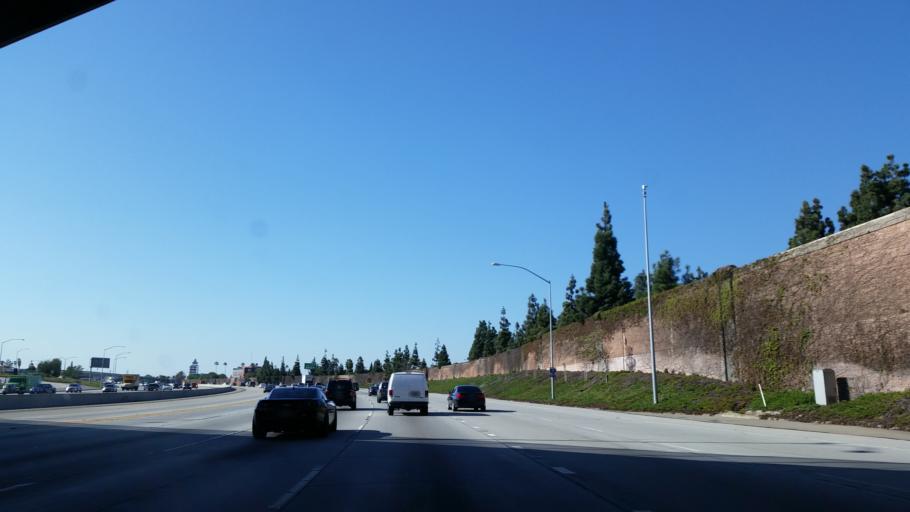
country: US
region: California
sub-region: Orange County
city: Anaheim
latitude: 33.8324
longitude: -117.9318
